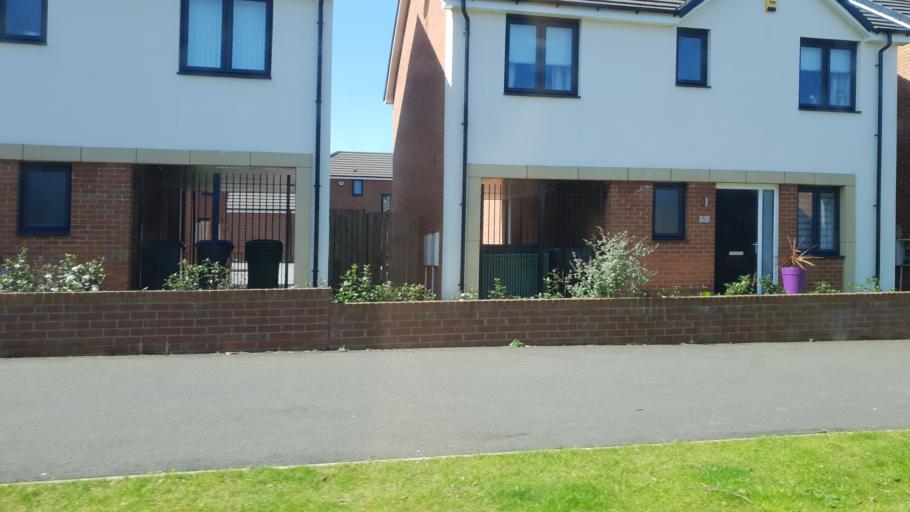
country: GB
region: England
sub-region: Middlesbrough
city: Nunthorpe
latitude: 54.5431
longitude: -1.2064
